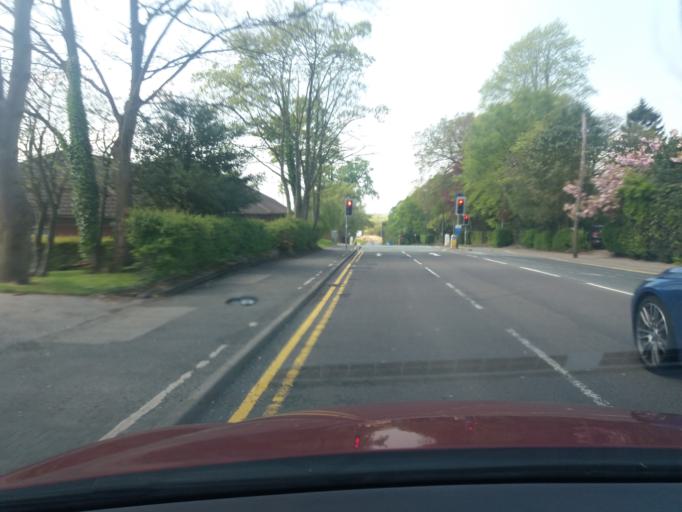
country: GB
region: England
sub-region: Lancashire
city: Chorley
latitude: 53.6669
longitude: -2.6349
